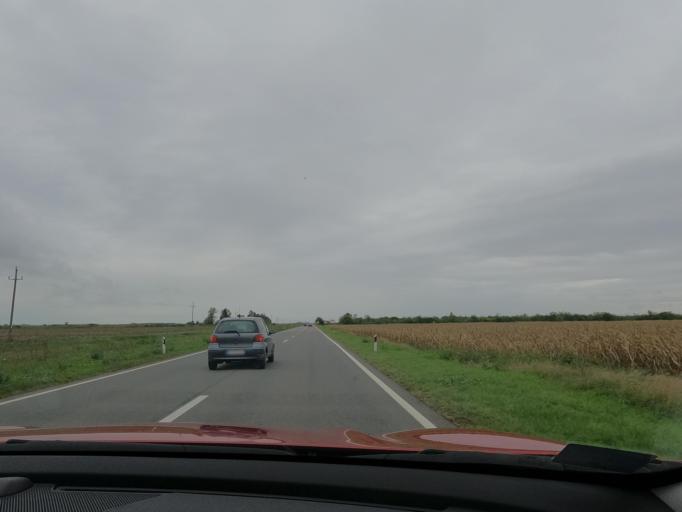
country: RS
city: Banatska Topola
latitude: 45.7158
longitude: 20.4179
